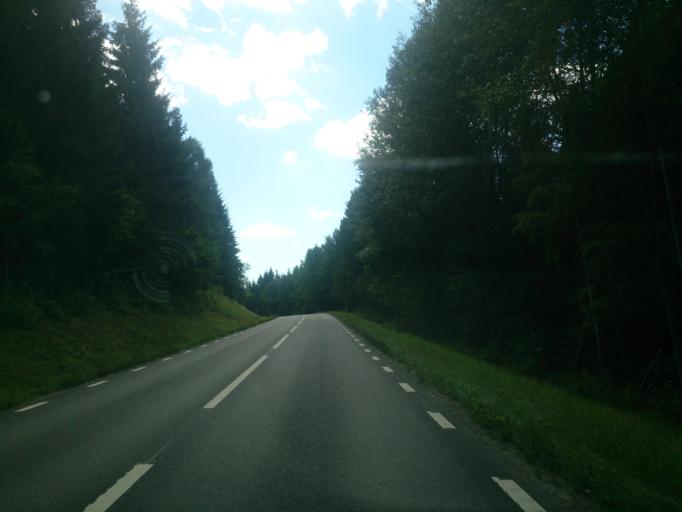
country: SE
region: OEstergoetland
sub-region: Atvidabergs Kommun
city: Atvidaberg
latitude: 58.1786
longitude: 16.0261
